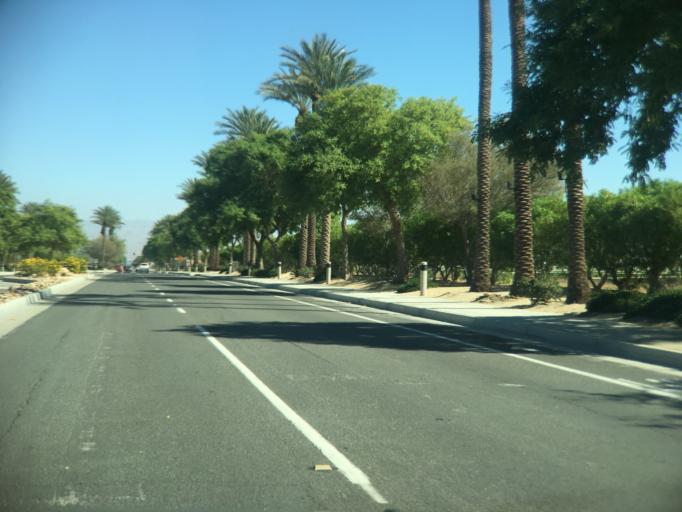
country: US
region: California
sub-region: Riverside County
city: Bermuda Dunes
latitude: 33.7216
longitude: -116.3027
